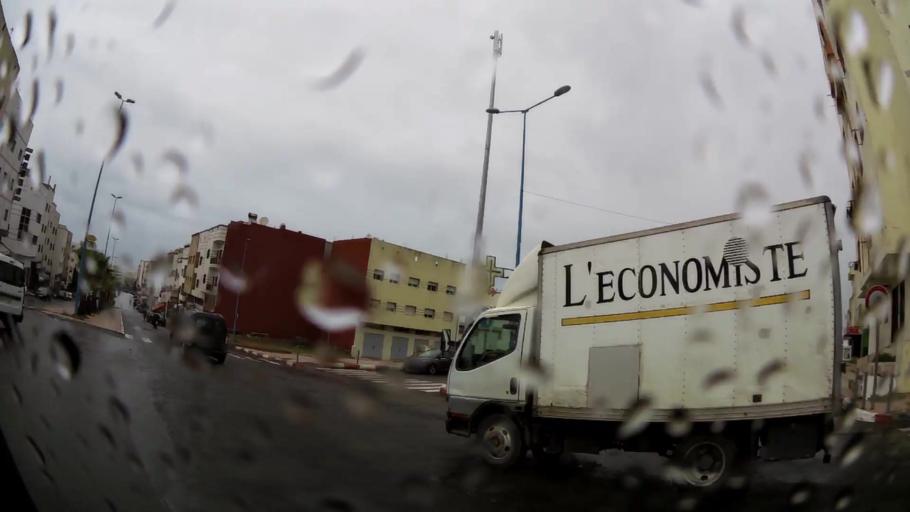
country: MA
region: Grand Casablanca
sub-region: Mediouna
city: Tit Mellil
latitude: 33.6183
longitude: -7.4855
